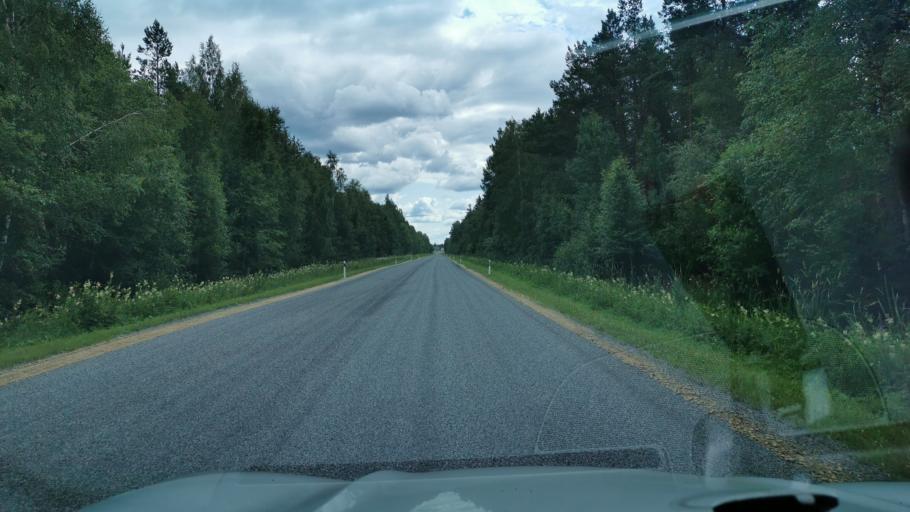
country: EE
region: Harju
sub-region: Anija vald
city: Kehra
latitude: 59.2398
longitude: 25.3709
